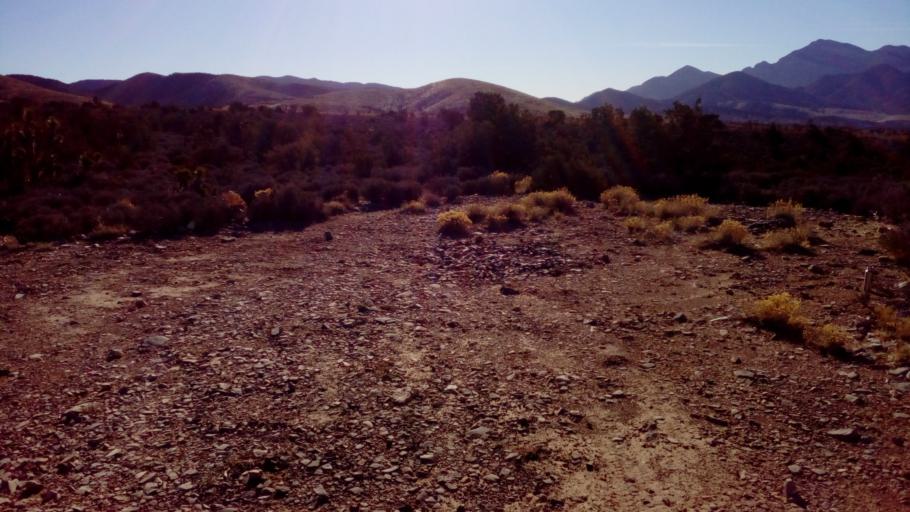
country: US
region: Nevada
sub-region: Clark County
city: Summerlin South
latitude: 36.0658
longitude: -115.5447
